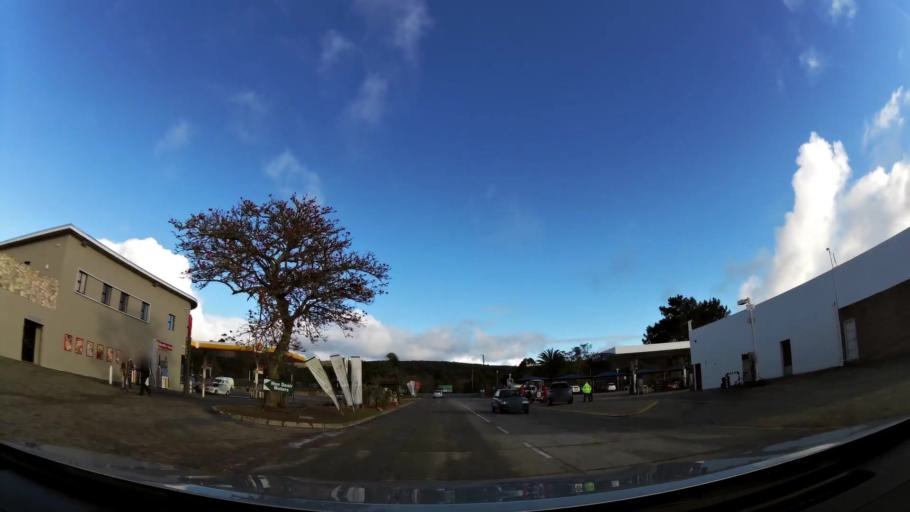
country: ZA
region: Western Cape
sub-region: Eden District Municipality
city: Riversdale
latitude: -34.2114
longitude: 21.5849
